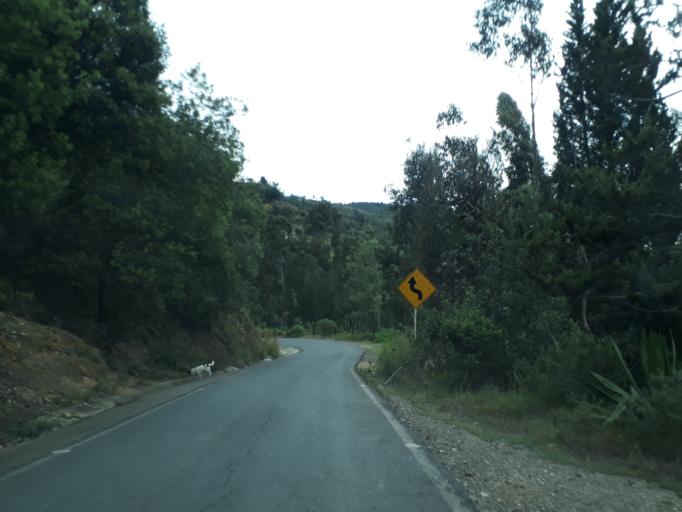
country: CO
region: Cundinamarca
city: Susa
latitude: 5.4007
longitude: -73.7689
